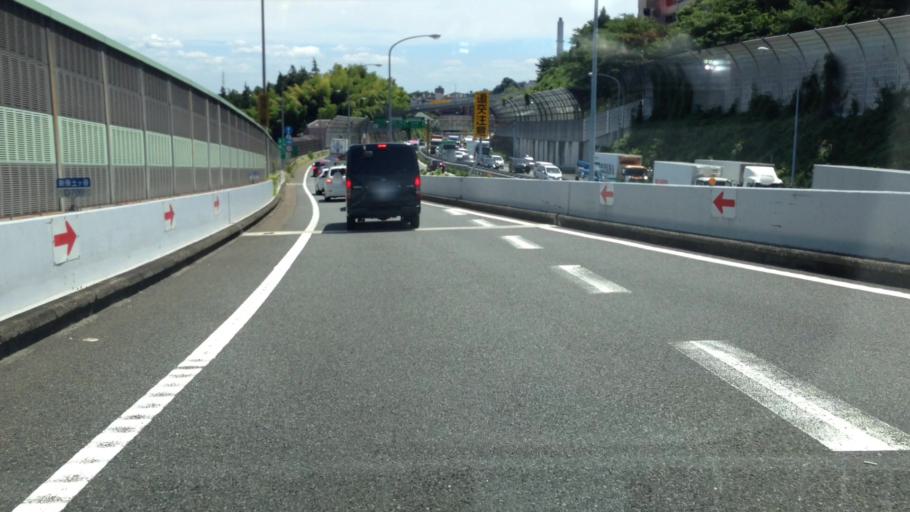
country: JP
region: Kanagawa
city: Yokohama
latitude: 35.4495
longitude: 139.5720
